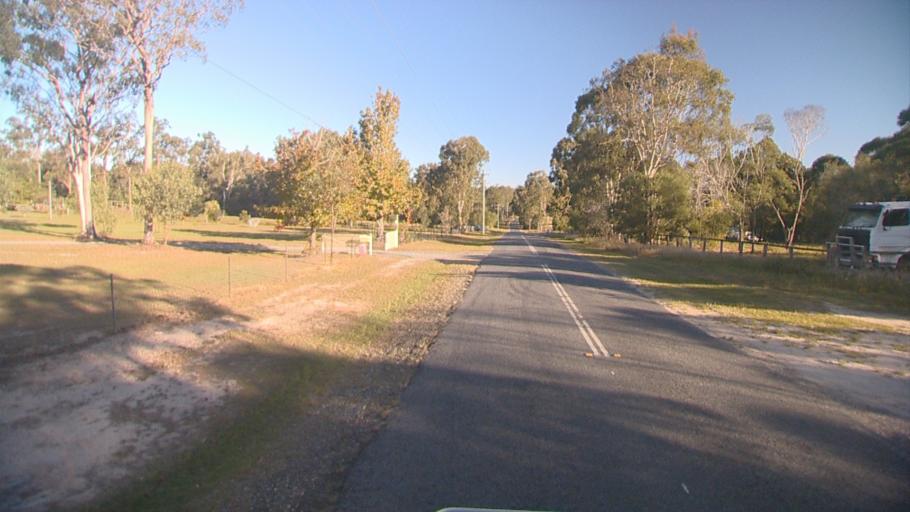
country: AU
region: Queensland
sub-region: Logan
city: Chambers Flat
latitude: -27.7734
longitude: 153.1293
